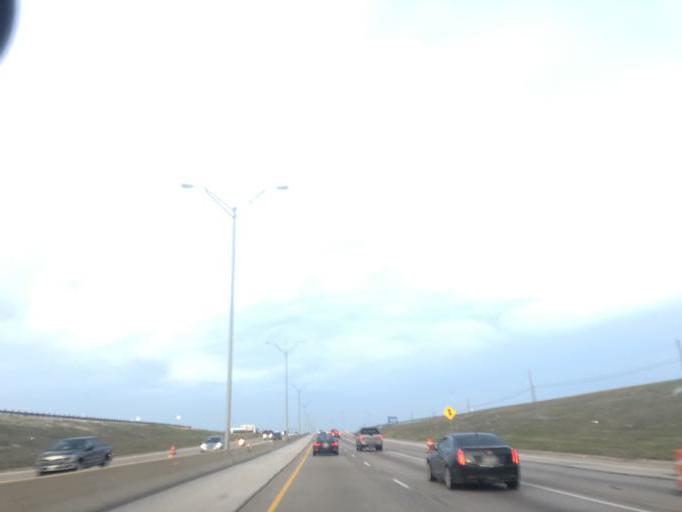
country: US
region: Texas
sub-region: Dallas County
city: Duncanville
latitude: 32.6713
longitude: -96.8617
